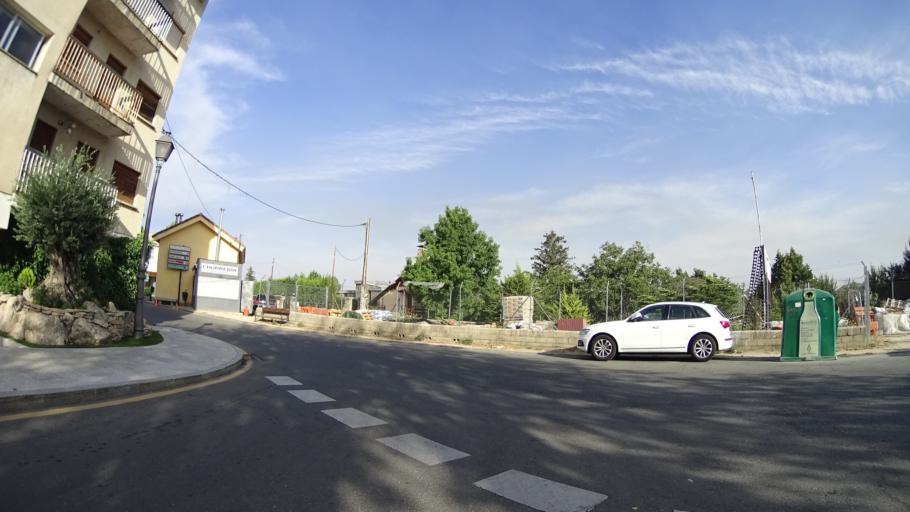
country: ES
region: Madrid
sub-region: Provincia de Madrid
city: Navacerrada
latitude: 40.7277
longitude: -4.0171
